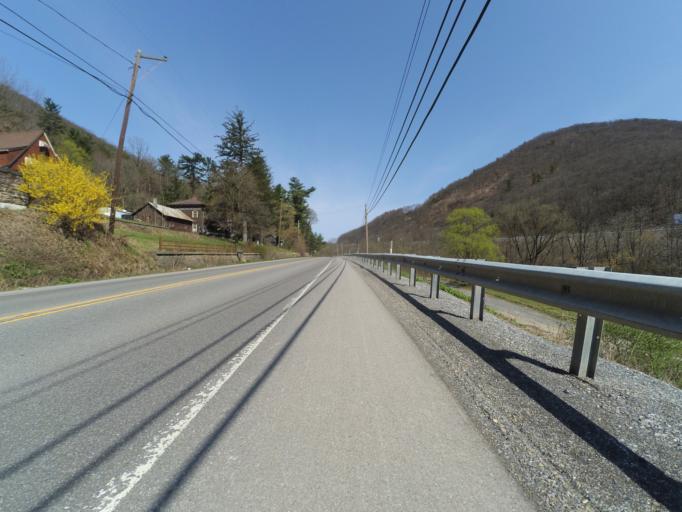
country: US
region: Pennsylvania
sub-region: Clinton County
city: Mill Hall
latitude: 41.0946
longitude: -77.4800
